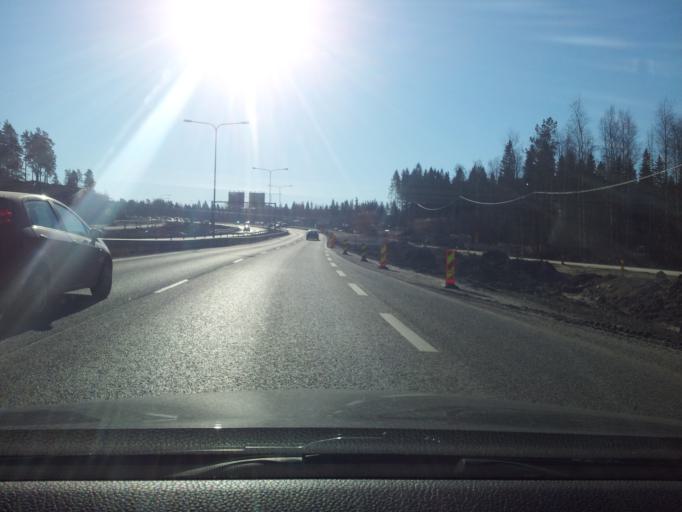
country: FI
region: Uusimaa
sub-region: Helsinki
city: Vantaa
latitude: 60.2330
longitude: 25.0492
